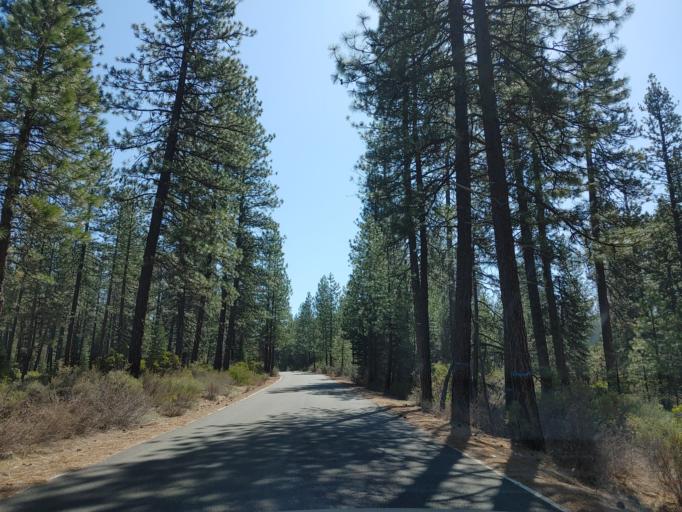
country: US
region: California
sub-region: Siskiyou County
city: McCloud
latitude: 41.2480
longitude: -122.0244
